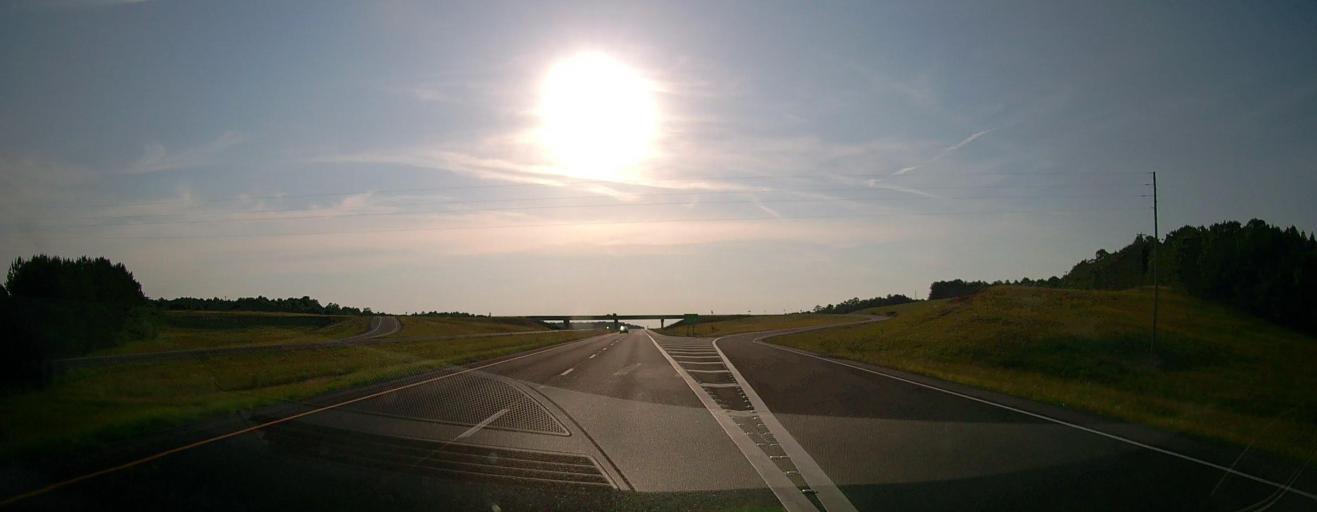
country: US
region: Alabama
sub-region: Marion County
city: Winfield
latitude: 33.9673
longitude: -87.7002
